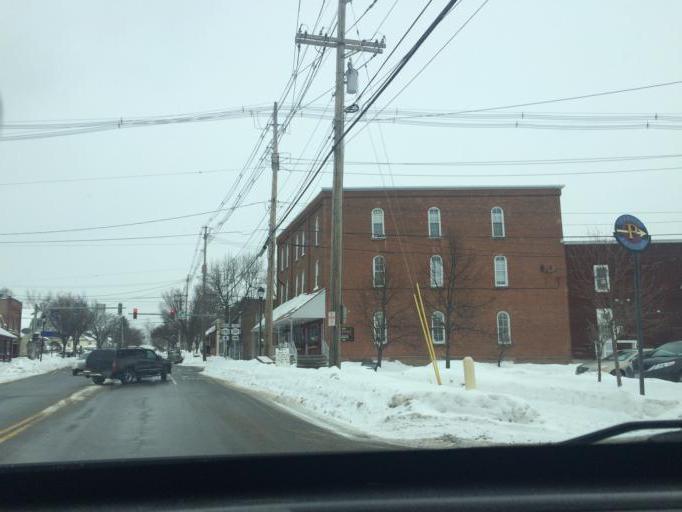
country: US
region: New York
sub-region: Monroe County
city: Fairport
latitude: 43.1042
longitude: -77.4418
